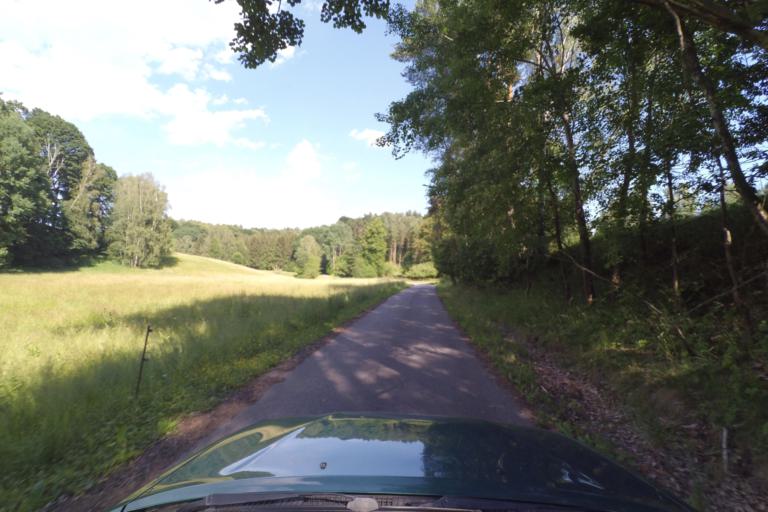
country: CZ
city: Osecna
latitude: 50.6714
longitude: 14.8814
